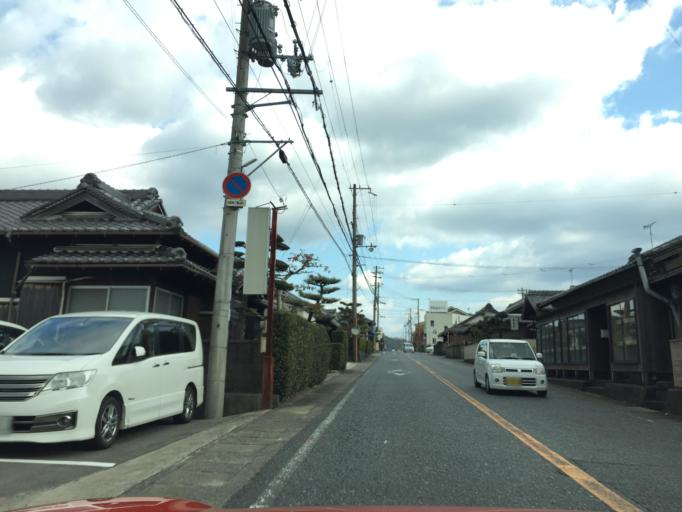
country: JP
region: Wakayama
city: Kainan
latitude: 34.1604
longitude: 135.2682
